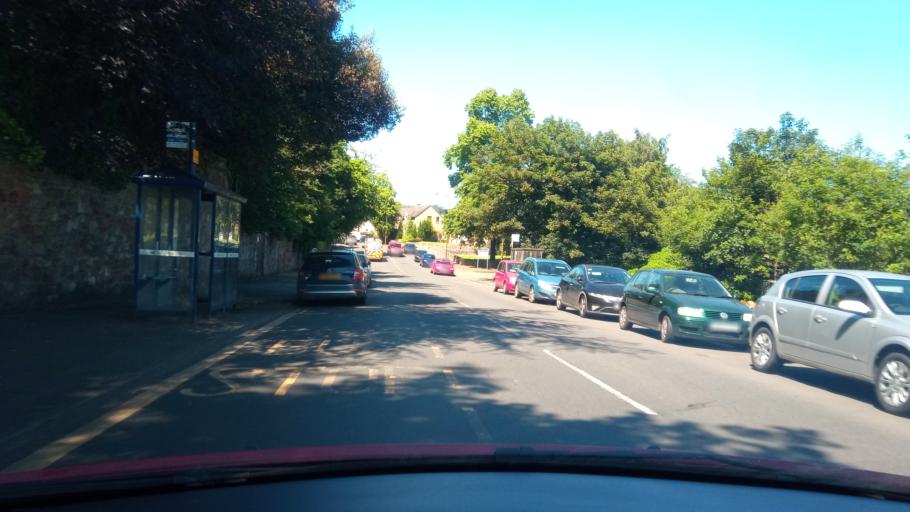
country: GB
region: Scotland
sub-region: East Lothian
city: Haddington
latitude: 55.9574
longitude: -2.7754
